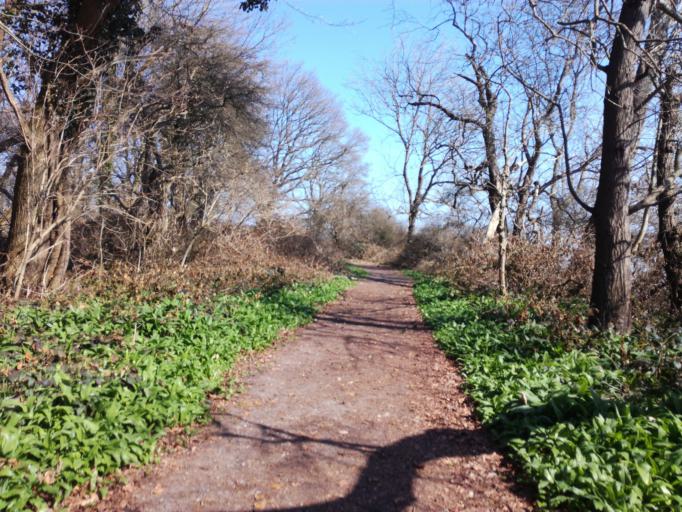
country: DK
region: South Denmark
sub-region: Fredericia Kommune
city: Fredericia
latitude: 55.6244
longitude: 9.8591
